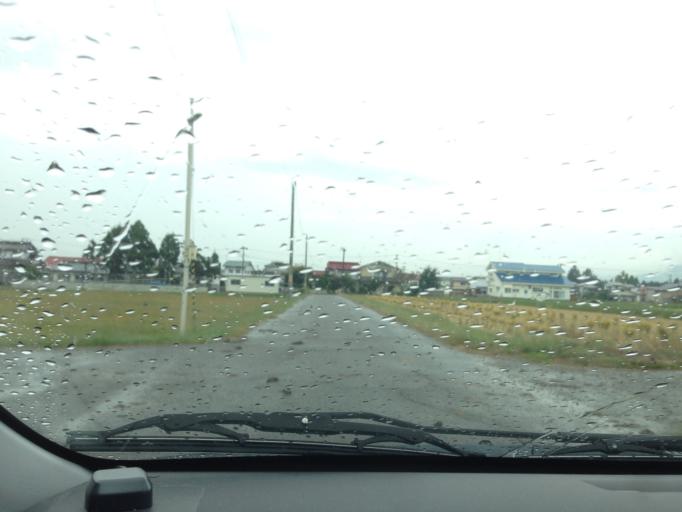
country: JP
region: Fukushima
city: Kitakata
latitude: 37.5221
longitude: 139.8307
